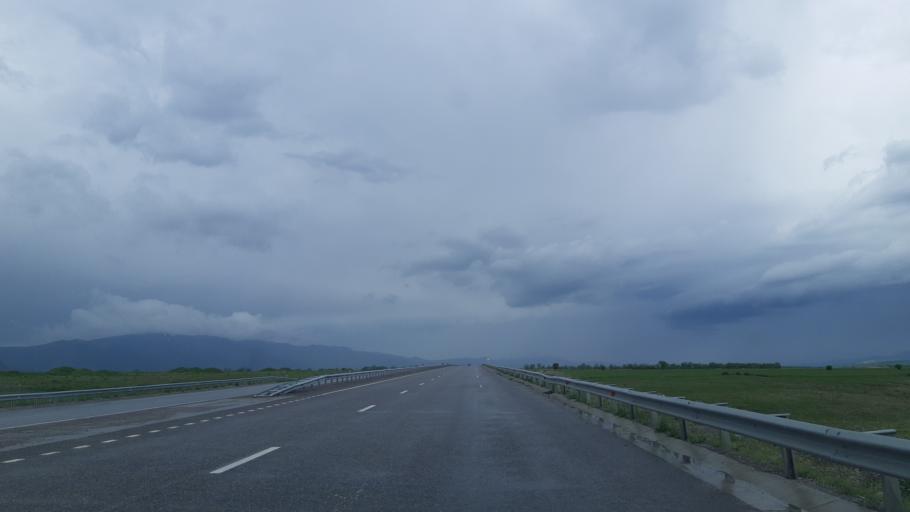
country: KZ
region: Ongtustik Qazaqstan
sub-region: Tulkibas Audany
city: Zhabagly
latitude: 42.5071
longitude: 70.4623
